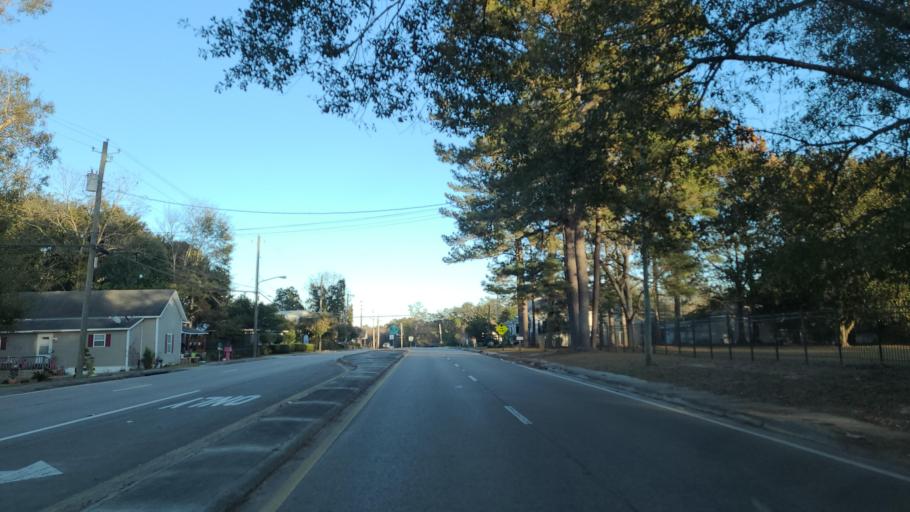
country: US
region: Mississippi
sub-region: Lamar County
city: Lumberton
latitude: 30.9992
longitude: -89.4445
